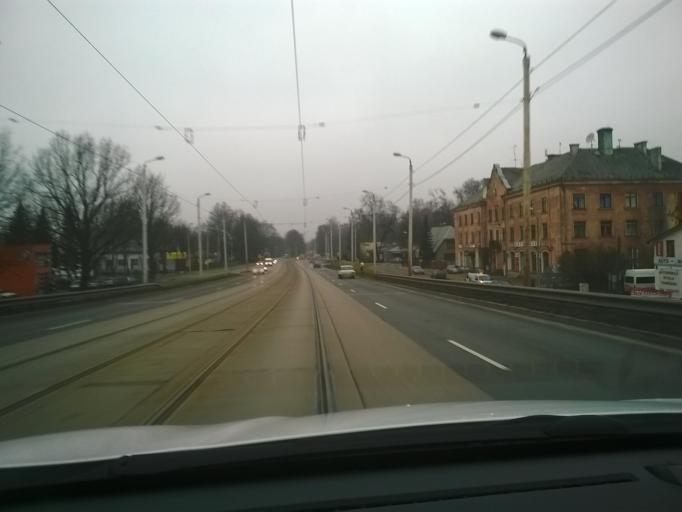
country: LV
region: Marupe
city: Marupe
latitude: 56.9520
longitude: 24.0410
